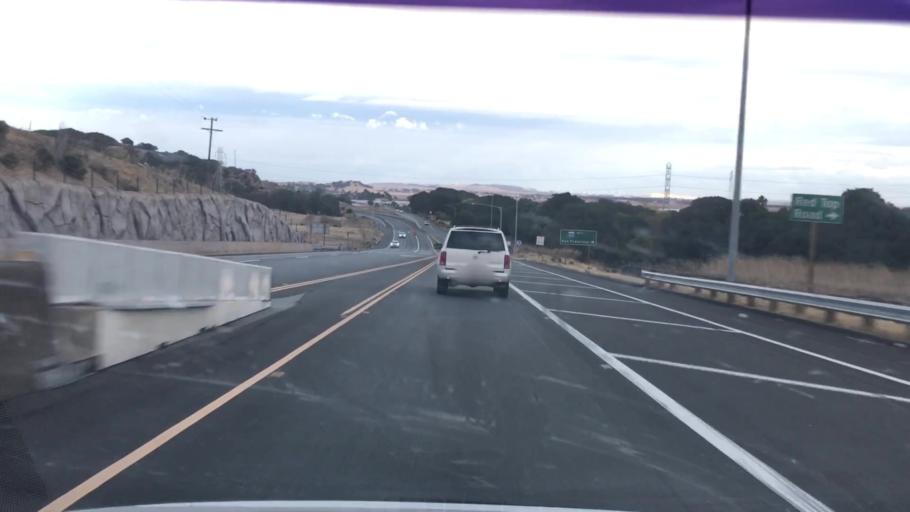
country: US
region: California
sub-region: Solano County
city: Green Valley
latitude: 38.2076
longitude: -122.1600
